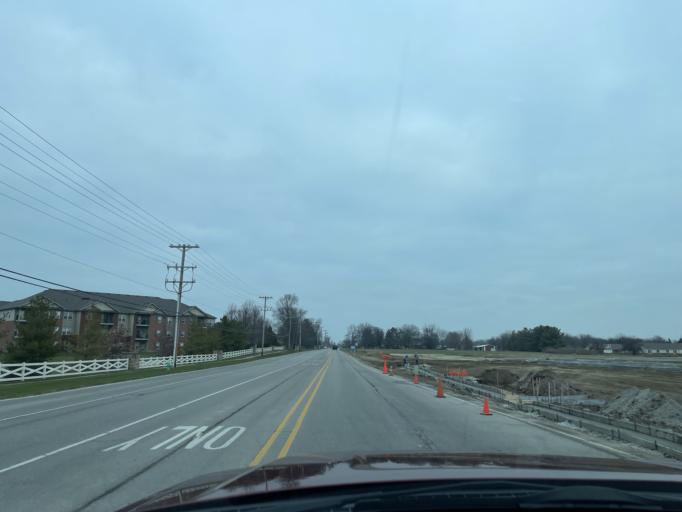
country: US
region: Indiana
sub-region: Hendricks County
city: Fairfield Heights
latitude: 39.8013
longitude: -86.4006
